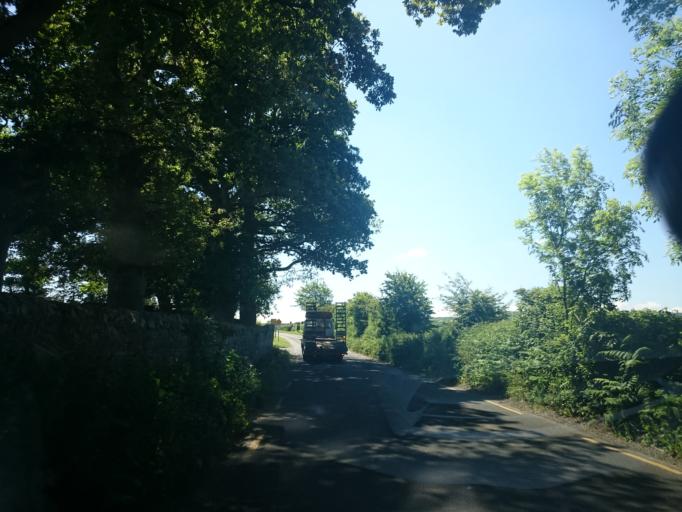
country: IE
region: Leinster
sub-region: Kilkenny
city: Graiguenamanagh
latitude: 52.6009
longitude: -6.9929
